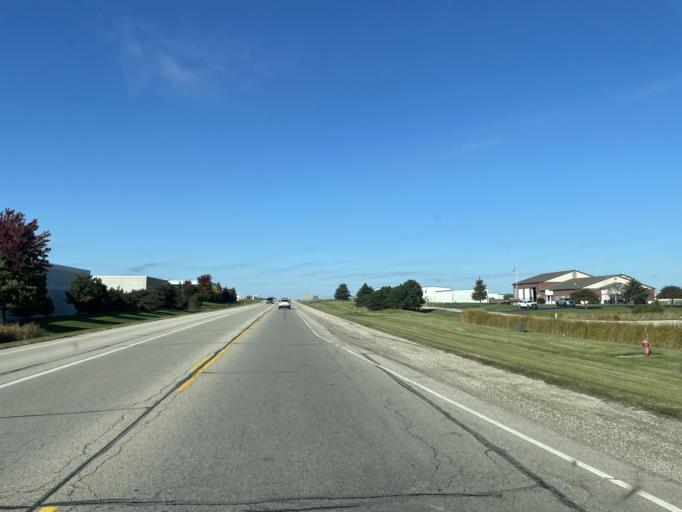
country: US
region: Wisconsin
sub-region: Kenosha County
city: Pleasant Prairie
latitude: 42.5894
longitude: -87.9242
